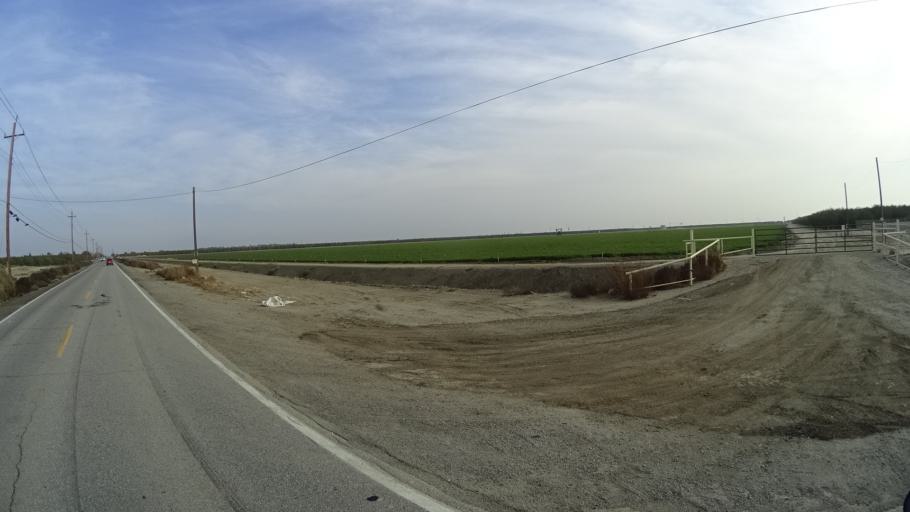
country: US
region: California
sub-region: Kern County
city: Rosedale
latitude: 35.2962
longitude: -119.1459
